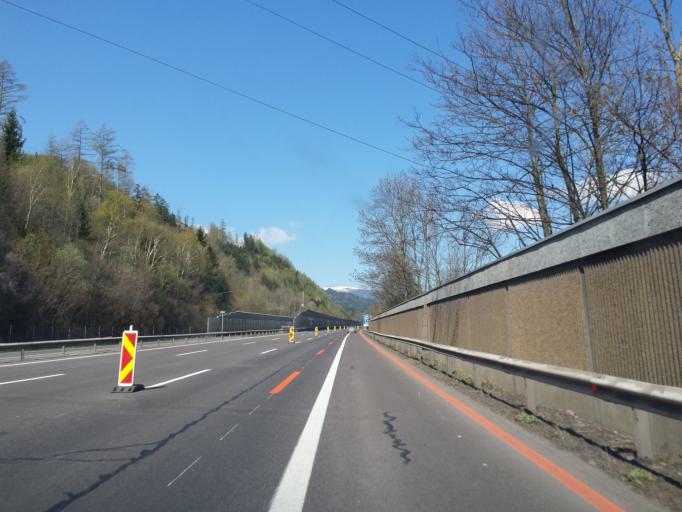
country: AT
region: Styria
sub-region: Politischer Bezirk Graz-Umgebung
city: Ubelbach
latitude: 47.2192
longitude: 15.2445
